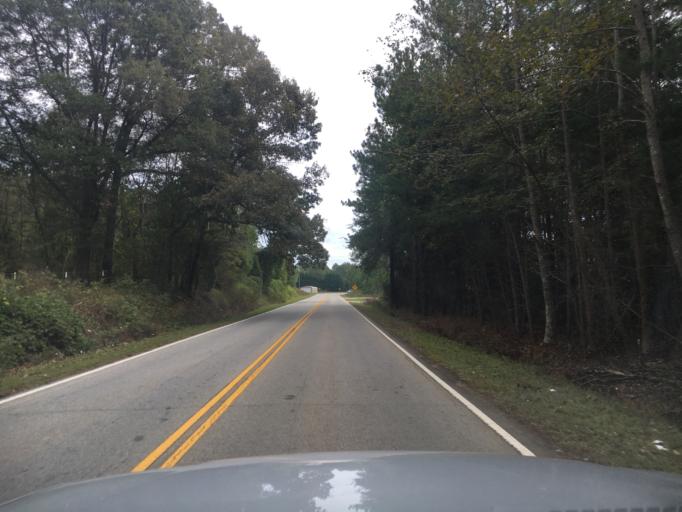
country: US
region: South Carolina
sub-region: Spartanburg County
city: Duncan
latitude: 34.9392
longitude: -82.1564
